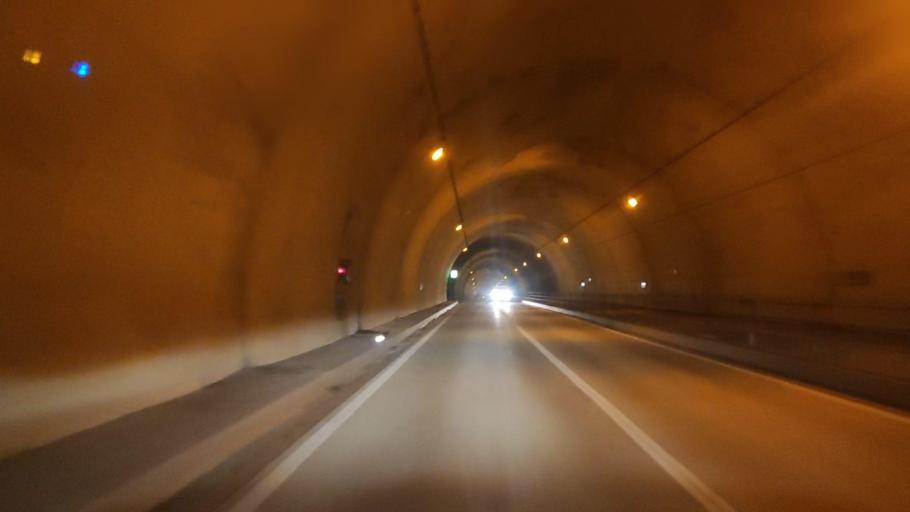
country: JP
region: Kumamoto
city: Hitoyoshi
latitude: 32.3908
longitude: 130.8294
